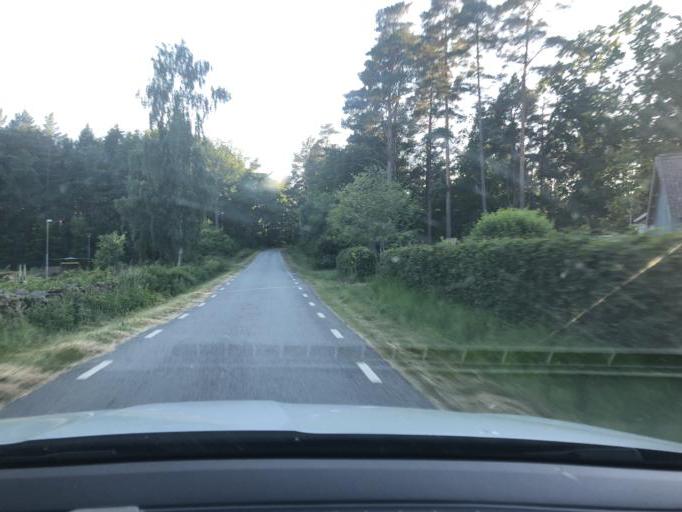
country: SE
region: Blekinge
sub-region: Solvesborgs Kommun
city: Soelvesborg
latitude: 56.1357
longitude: 14.6189
